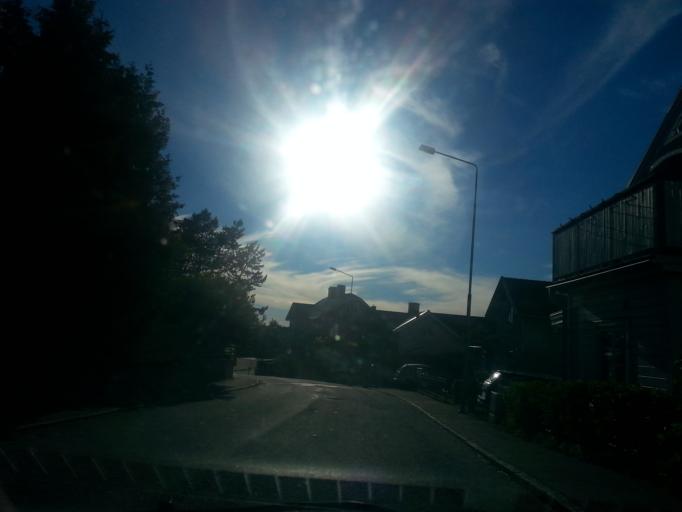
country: SE
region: Vaestra Goetaland
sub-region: Molndal
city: Moelndal
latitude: 57.6537
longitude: 12.0334
